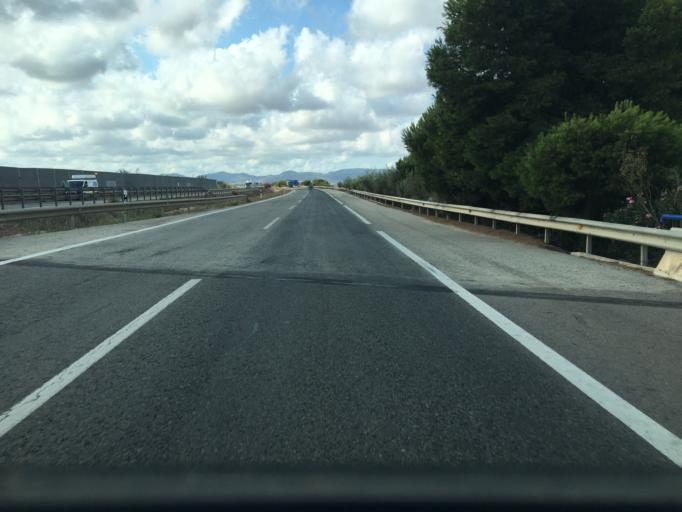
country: ES
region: Murcia
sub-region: Murcia
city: Los Alcazares
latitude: 37.7188
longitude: -0.8700
